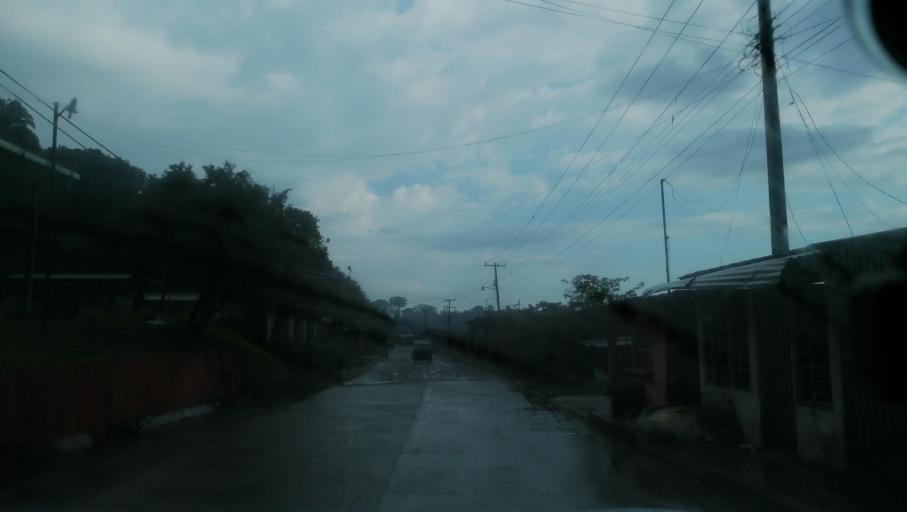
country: MX
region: Chiapas
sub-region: Cacahoatan
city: Benito Juarez
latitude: 15.0551
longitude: -92.1914
